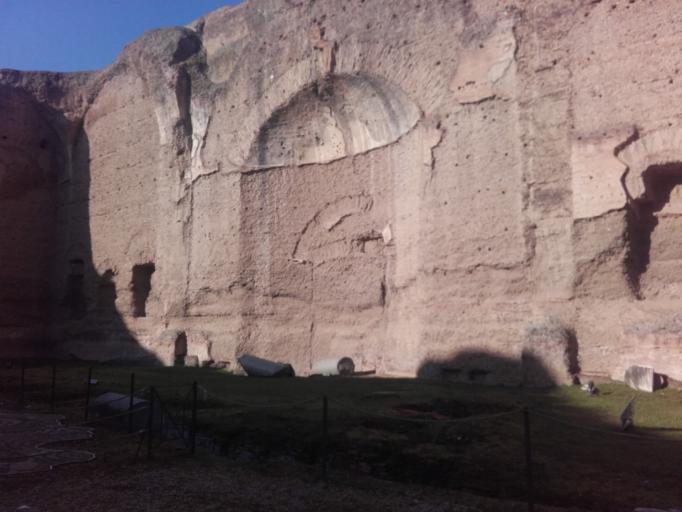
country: IT
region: Latium
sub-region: Citta metropolitana di Roma Capitale
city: Rome
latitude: 41.8801
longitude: 12.4925
